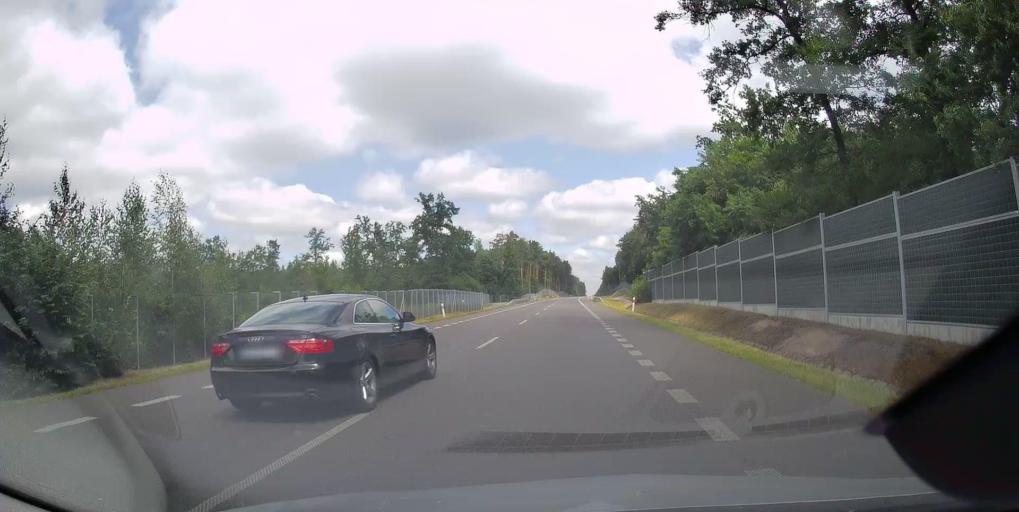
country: PL
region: Subcarpathian Voivodeship
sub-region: Powiat mielecki
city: Przeclaw
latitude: 50.2616
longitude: 21.4929
